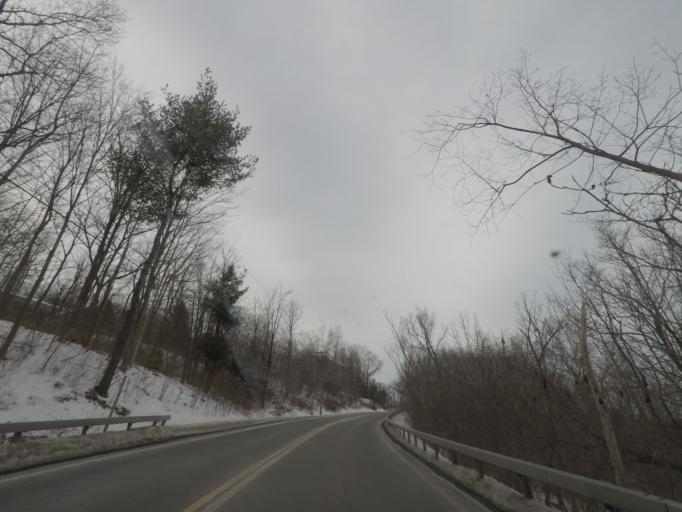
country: US
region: New York
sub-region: Albany County
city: Altamont
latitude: 42.7017
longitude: -74.0361
